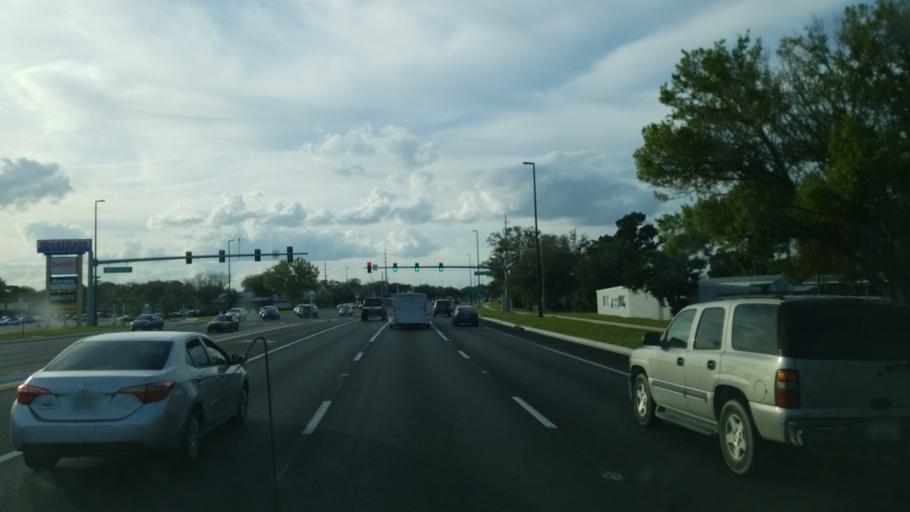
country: US
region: Florida
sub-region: Osceola County
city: Saint Cloud
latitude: 28.2473
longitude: -81.3065
